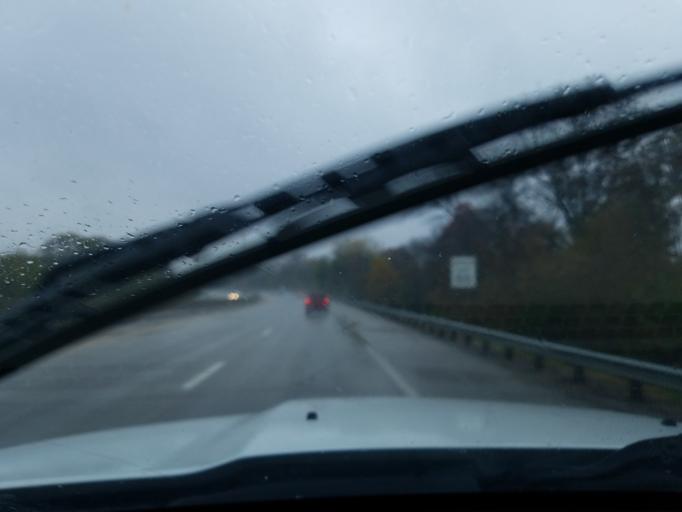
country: US
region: Indiana
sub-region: Floyd County
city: New Albany
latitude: 38.2696
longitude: -85.8084
